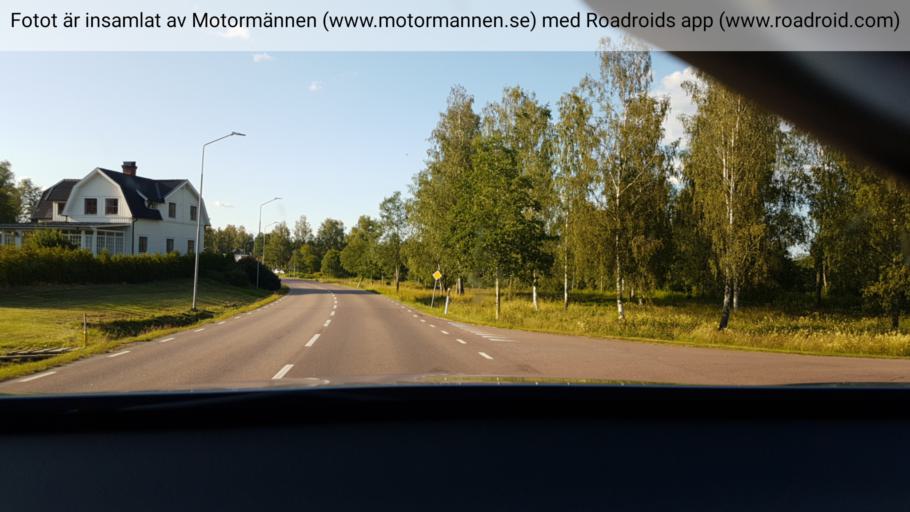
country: SE
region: Vaermland
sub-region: Forshaga Kommun
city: Forshaga
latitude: 59.5456
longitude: 13.4812
